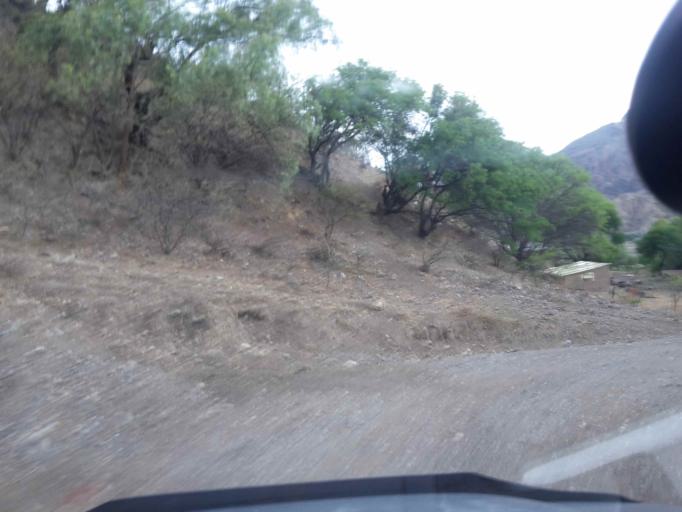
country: BO
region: Cochabamba
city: Sipe Sipe
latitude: -17.5322
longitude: -66.5151
